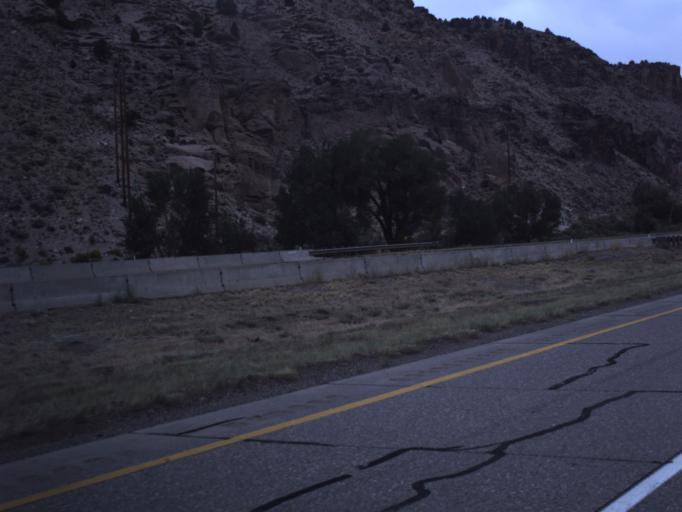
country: US
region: Utah
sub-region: Sevier County
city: Monroe
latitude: 38.5782
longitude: -112.3146
